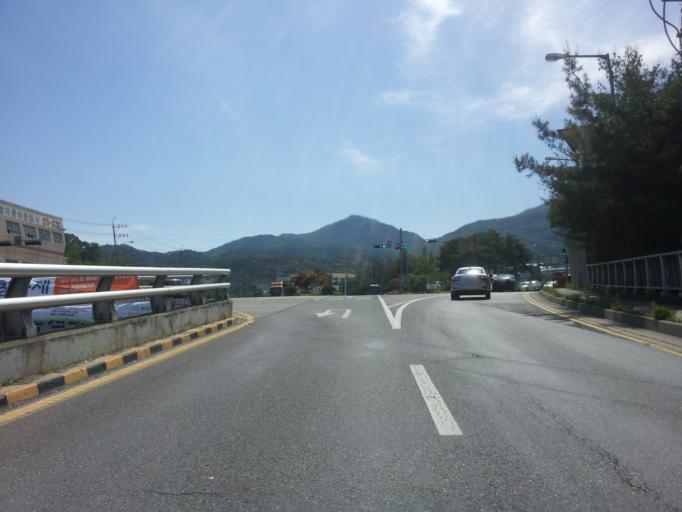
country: KR
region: Daejeon
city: Daejeon
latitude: 36.3185
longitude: 127.4652
